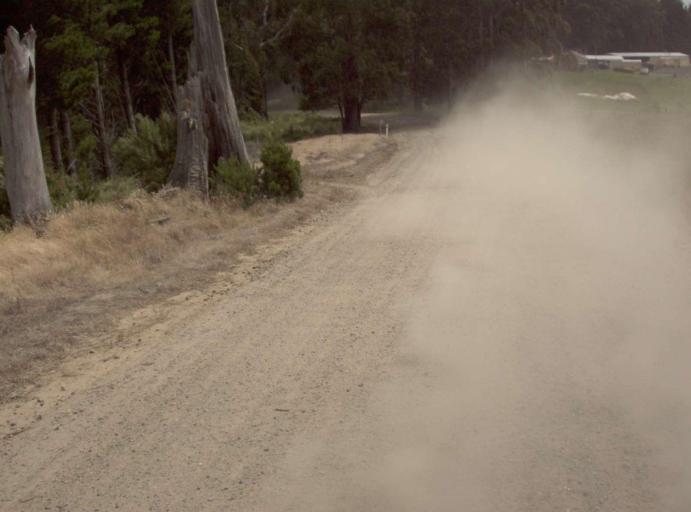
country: AU
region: Victoria
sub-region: Latrobe
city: Traralgon
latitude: -38.3790
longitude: 146.6693
